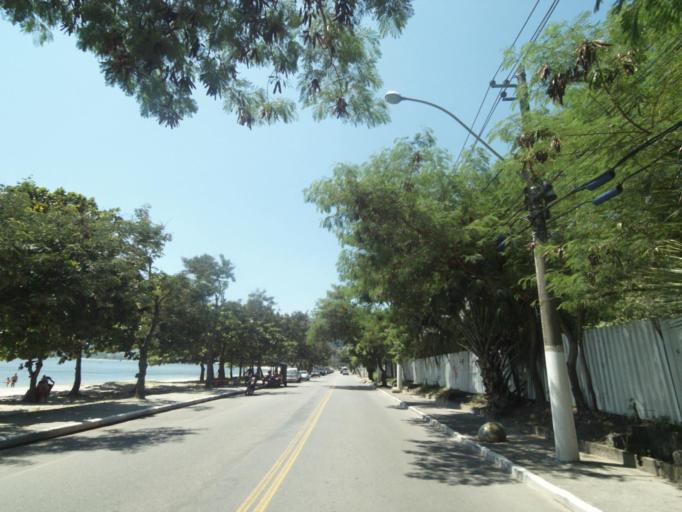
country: BR
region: Rio de Janeiro
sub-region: Niteroi
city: Niteroi
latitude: -22.9359
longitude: -43.1046
